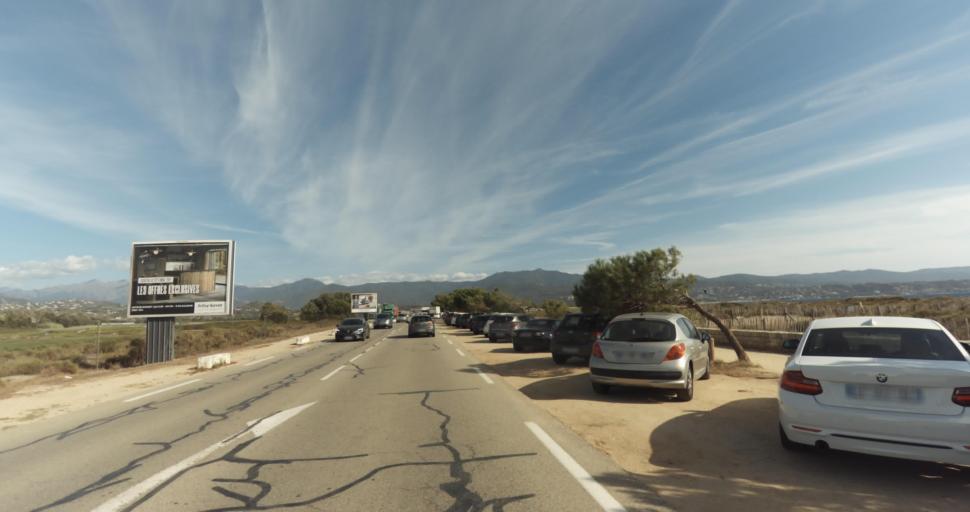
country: FR
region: Corsica
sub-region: Departement de la Corse-du-Sud
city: Ajaccio
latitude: 41.9249
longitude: 8.7819
